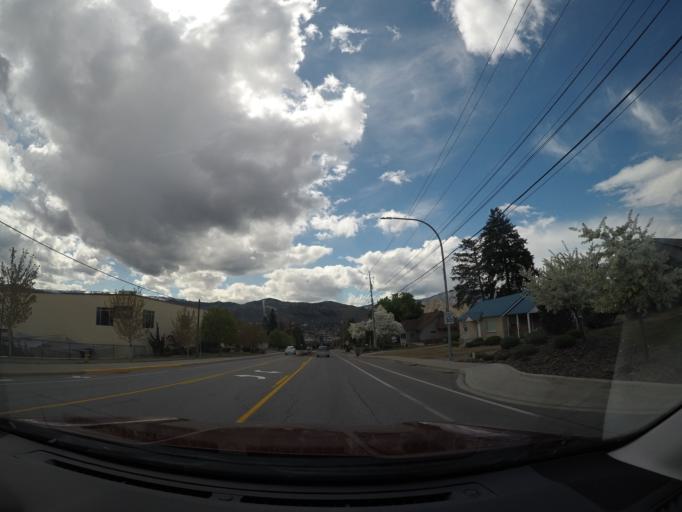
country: US
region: Washington
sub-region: Douglas County
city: East Wenatchee
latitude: 47.4173
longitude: -120.2875
